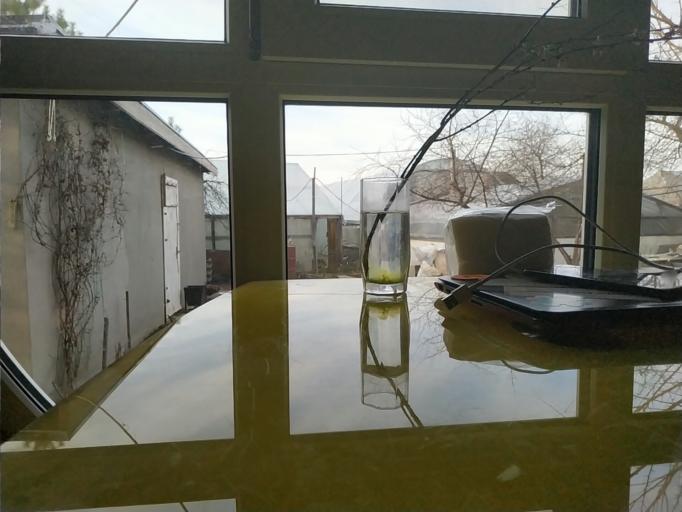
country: RU
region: Republic of Karelia
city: Suoyarvi
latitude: 61.8385
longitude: 32.2835
